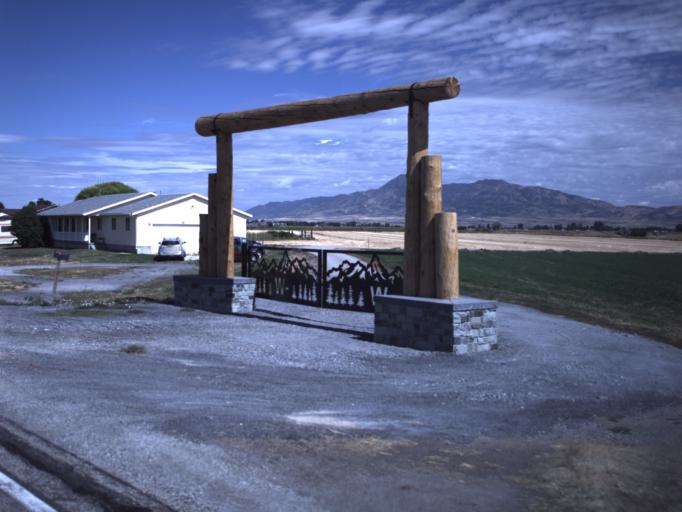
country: US
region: Utah
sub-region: Box Elder County
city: Garland
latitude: 41.7450
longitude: -112.1454
